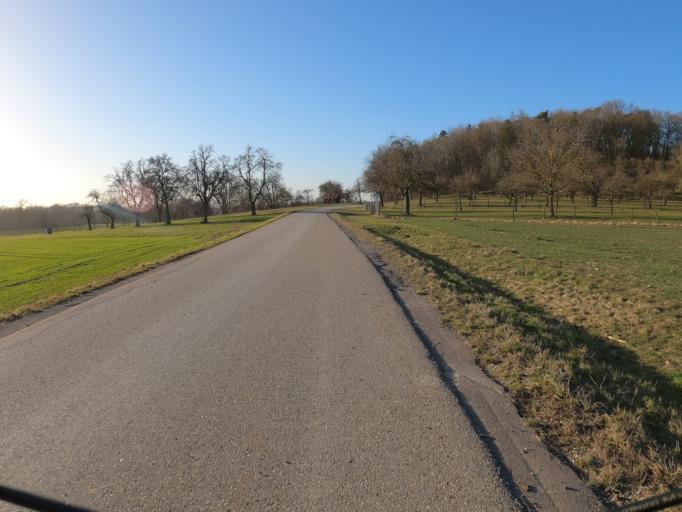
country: DE
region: Bavaria
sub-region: Swabia
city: Holzheim
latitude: 48.4055
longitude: 10.0989
